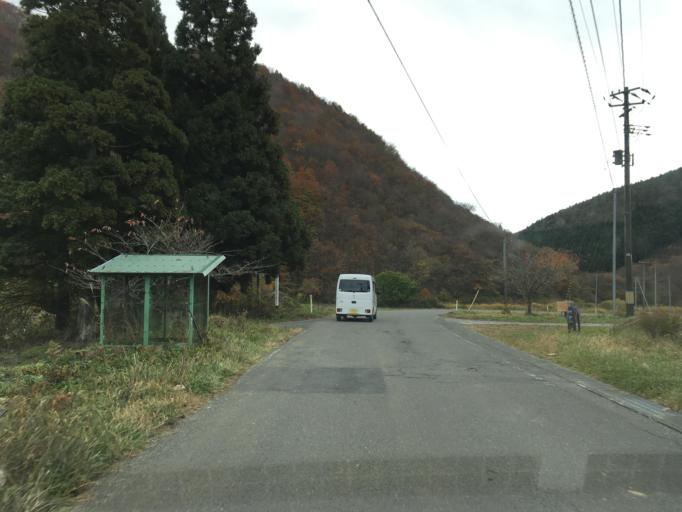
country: JP
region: Iwate
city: Mizusawa
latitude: 39.1065
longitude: 141.3289
